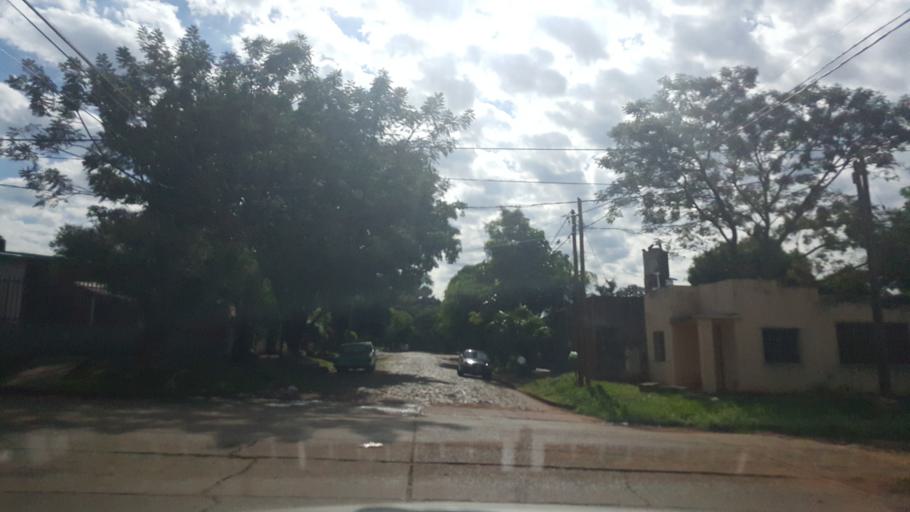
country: AR
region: Misiones
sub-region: Departamento de Capital
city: Posadas
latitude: -27.3672
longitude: -55.9184
